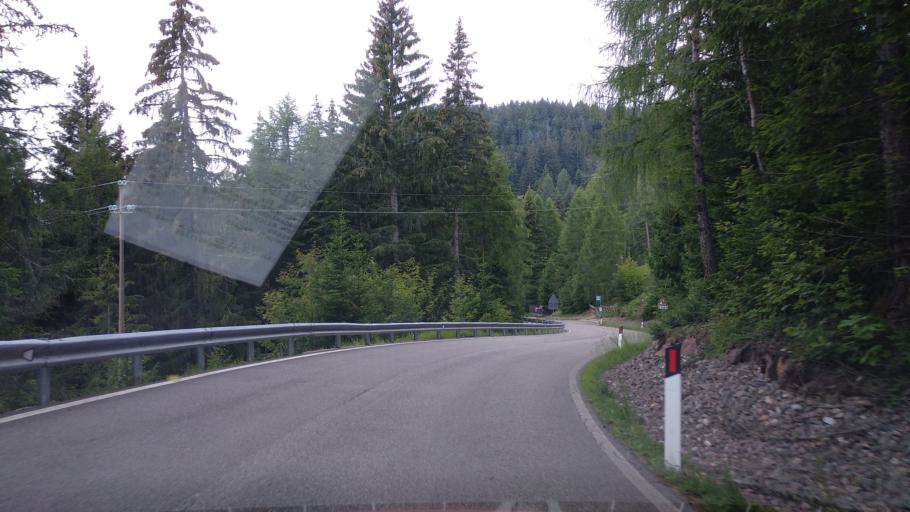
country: IT
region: Trentino-Alto Adige
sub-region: Bolzano
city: Avelengo
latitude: 46.6566
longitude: 11.2286
